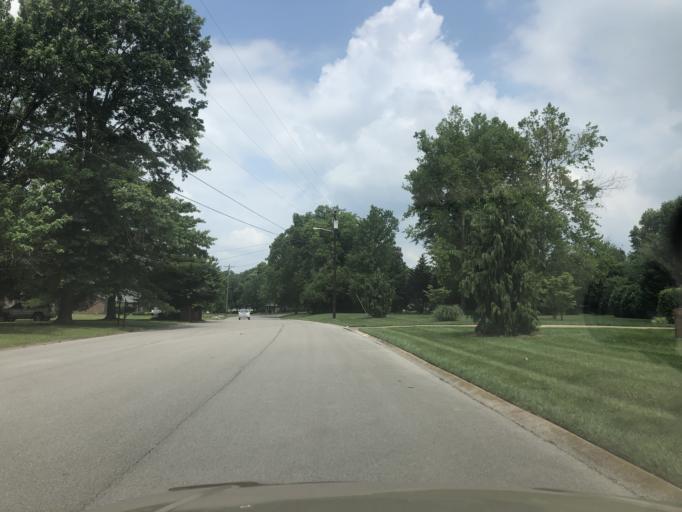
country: US
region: Tennessee
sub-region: Davidson County
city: Lakewood
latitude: 36.2397
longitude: -86.6153
